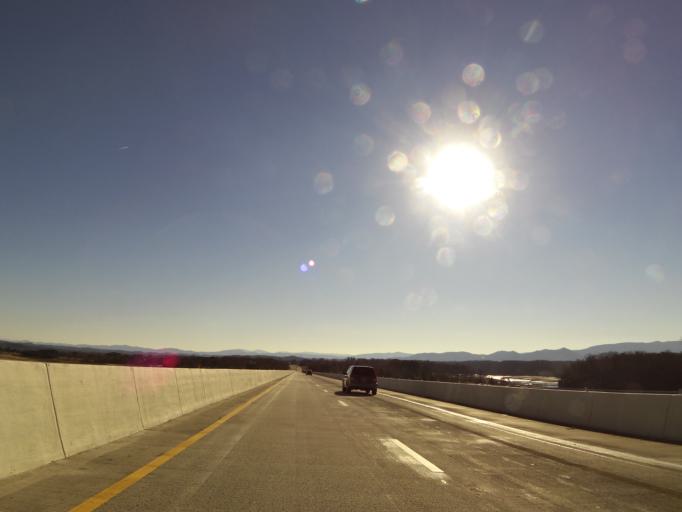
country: US
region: Tennessee
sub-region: Jefferson County
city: Dandridge
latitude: 36.0429
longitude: -83.3385
